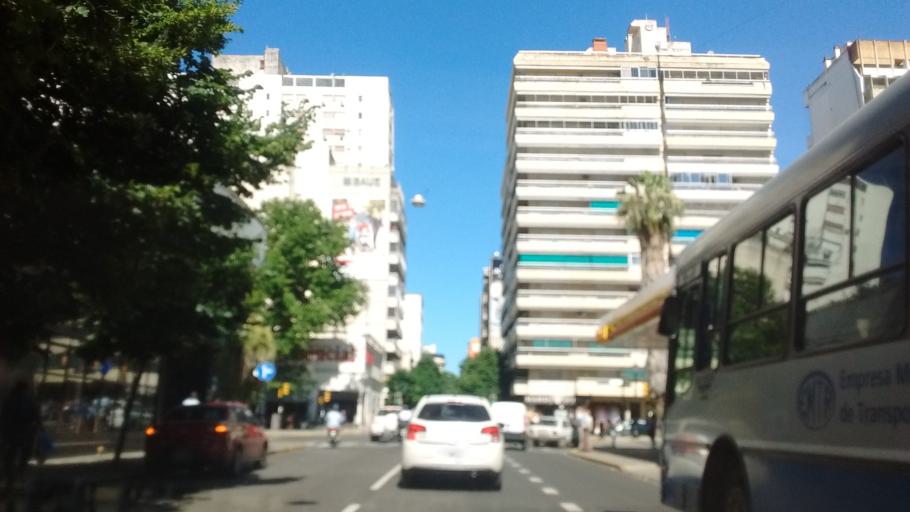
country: AR
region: Santa Fe
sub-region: Departamento de Rosario
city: Rosario
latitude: -32.9437
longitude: -60.6537
